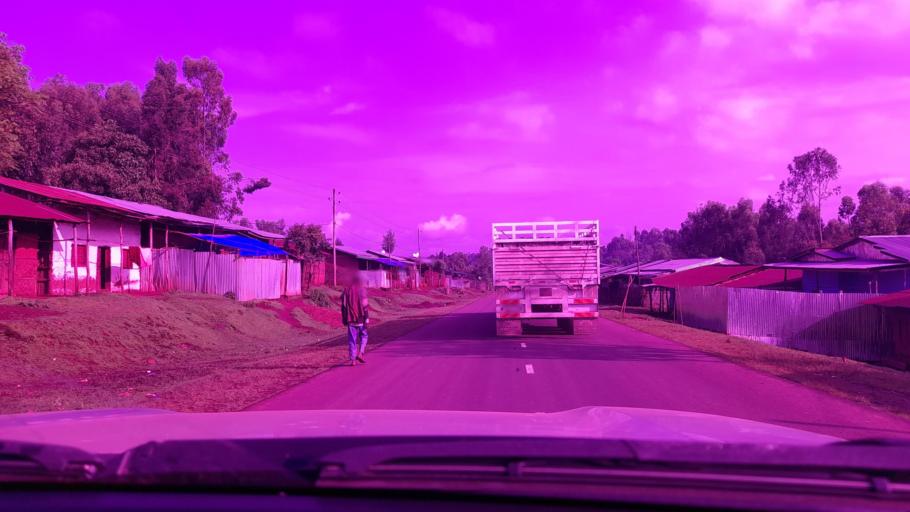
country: ET
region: Oromiya
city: Bedele
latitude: 8.1778
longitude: 36.4569
